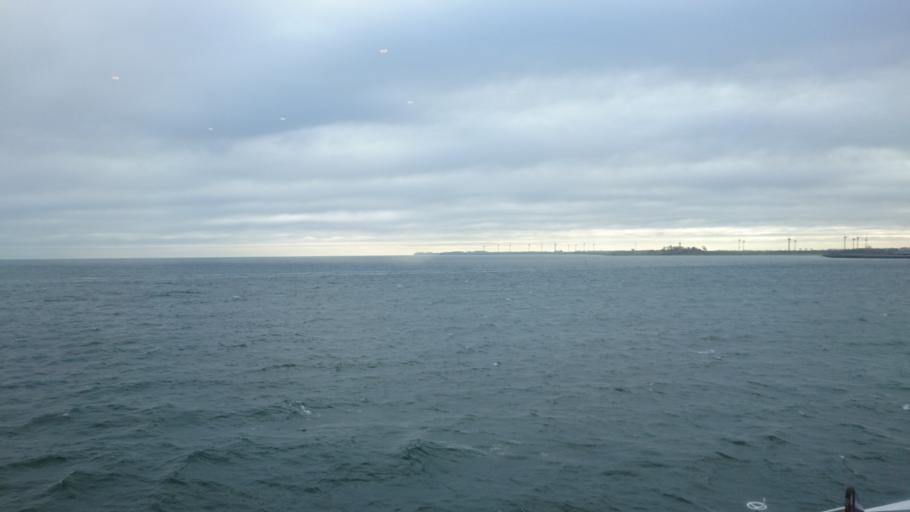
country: DE
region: Schleswig-Holstein
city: Fehmarn
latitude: 54.5165
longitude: 11.2373
